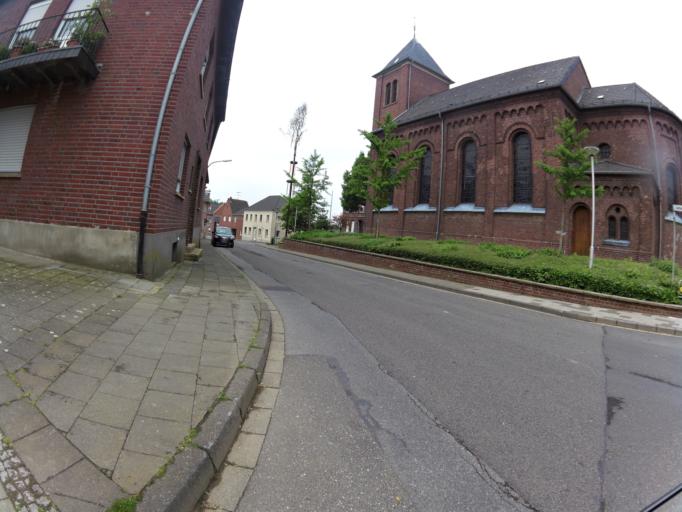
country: DE
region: North Rhine-Westphalia
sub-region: Regierungsbezirk Koln
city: Heinsberg
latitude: 51.0210
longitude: 6.1346
